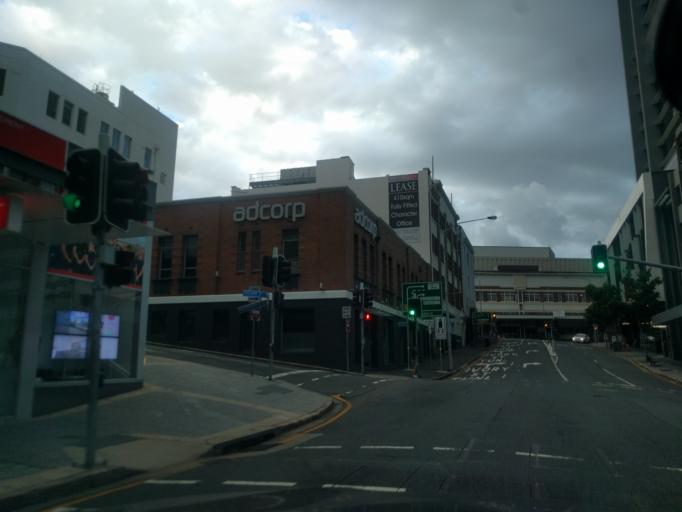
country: AU
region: Queensland
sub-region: Brisbane
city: Fortitude Valley
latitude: -27.4628
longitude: 153.0320
